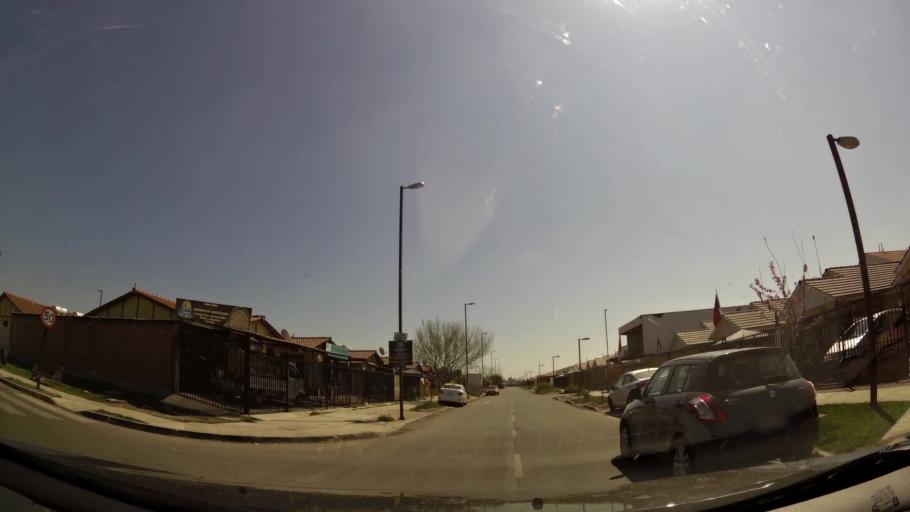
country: CL
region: Santiago Metropolitan
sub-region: Provincia de Chacabuco
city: Lampa
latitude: -33.3251
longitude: -70.7660
